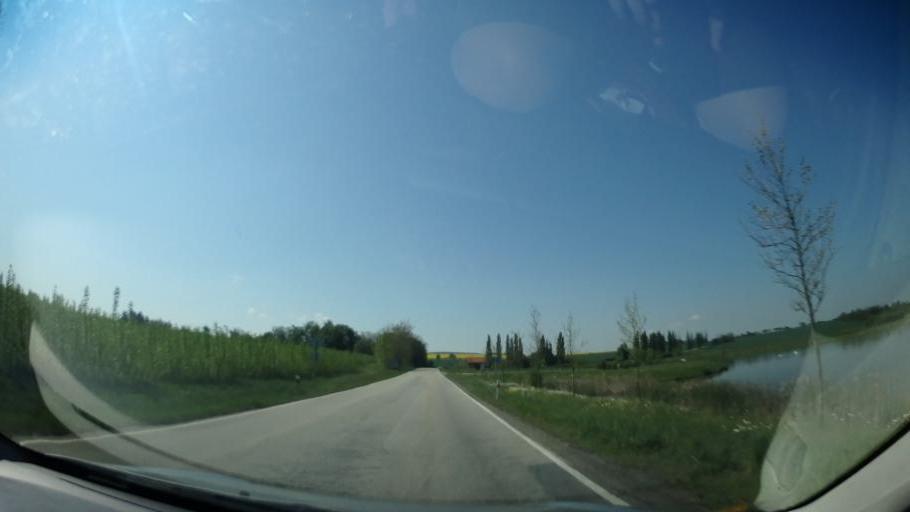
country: CZ
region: Vysocina
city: Namest' nad Oslavou
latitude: 49.2111
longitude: 16.1195
